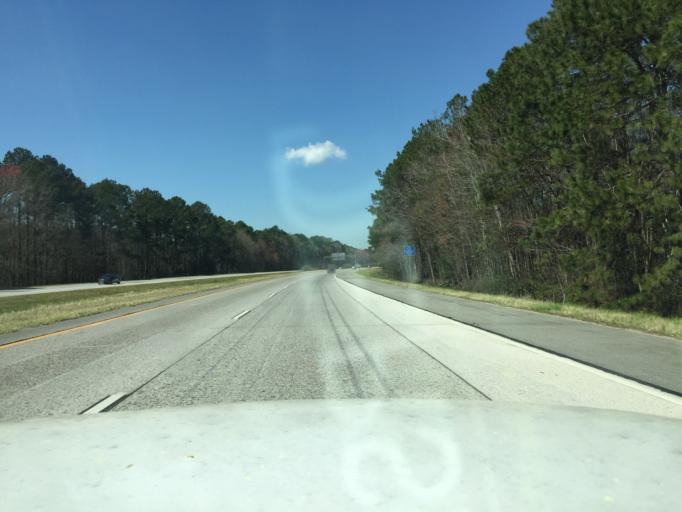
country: US
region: Georgia
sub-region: Chatham County
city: Pooler
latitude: 32.0751
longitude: -81.2534
